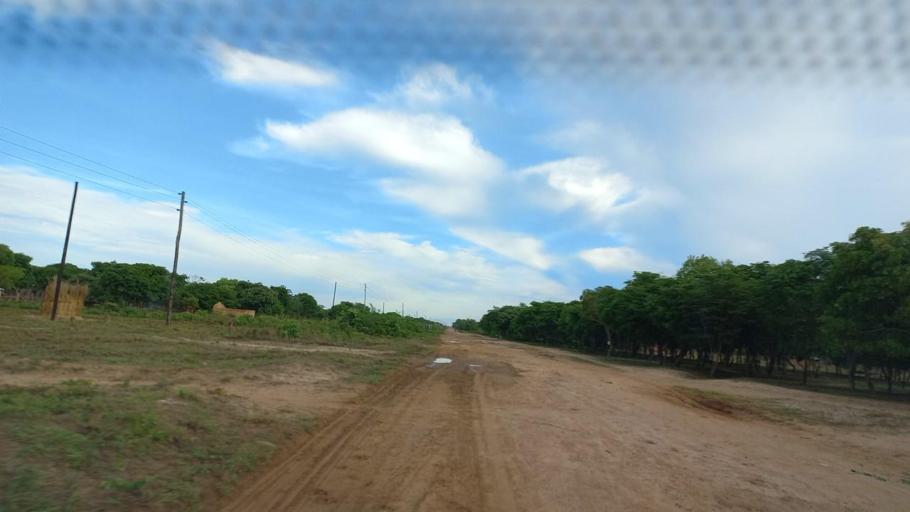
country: ZM
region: North-Western
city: Kabompo
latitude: -13.4276
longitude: 24.3270
